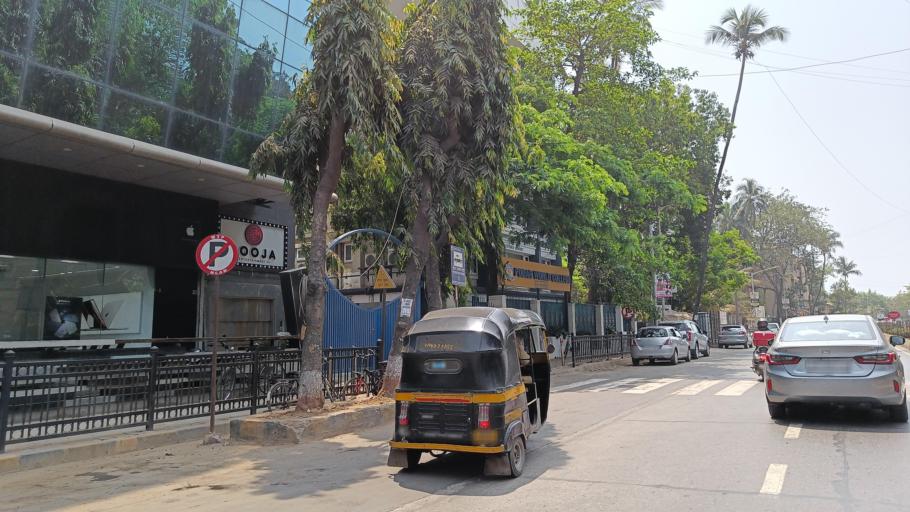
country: IN
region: Maharashtra
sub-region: Mumbai Suburban
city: Mumbai
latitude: 19.1004
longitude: 72.8274
